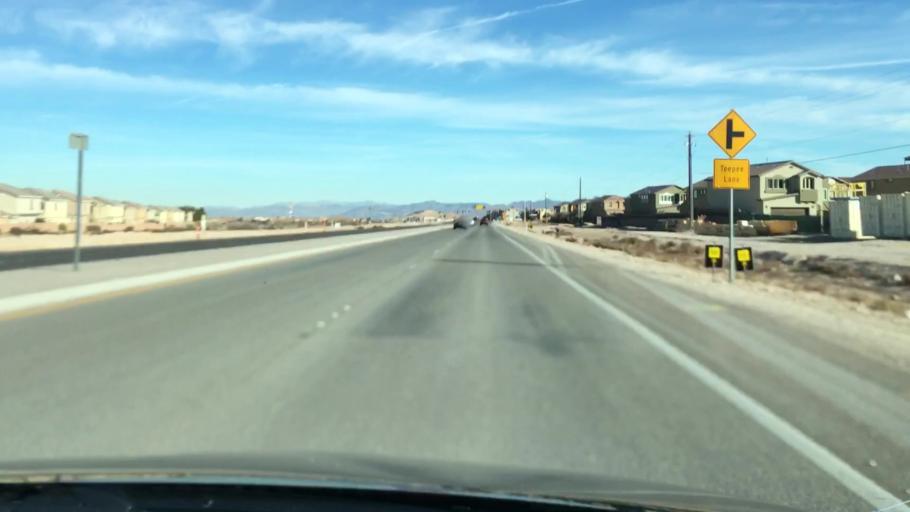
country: US
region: Nevada
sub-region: Clark County
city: Enterprise
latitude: 36.0213
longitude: -115.3048
